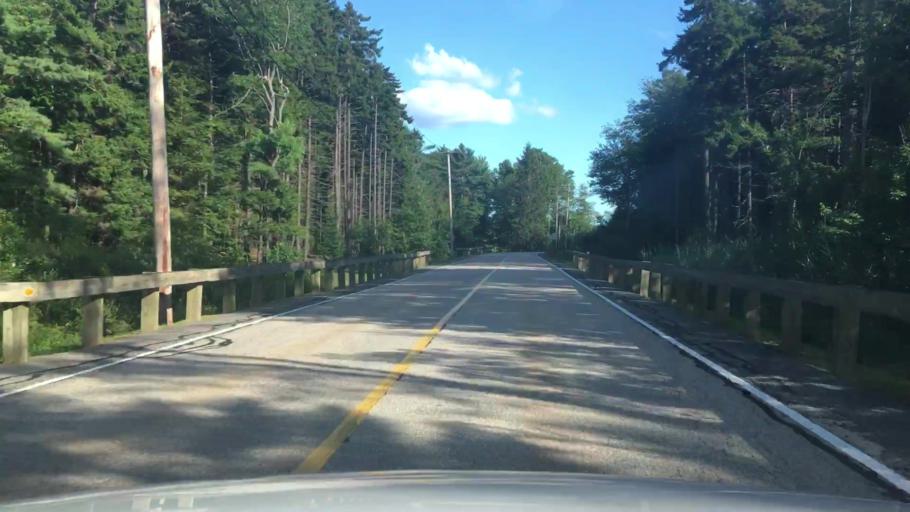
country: US
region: Maine
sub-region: Cumberland County
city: Scarborough
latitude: 43.5621
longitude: -70.2889
